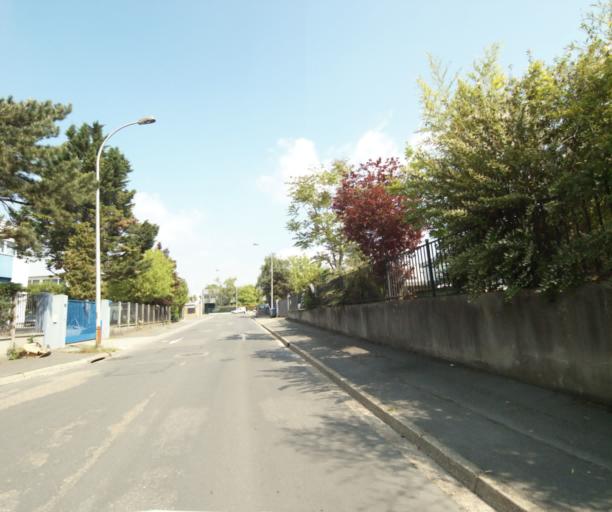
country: FR
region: Ile-de-France
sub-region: Departement du Val-d'Oise
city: Bezons
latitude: 48.9480
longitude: 2.2190
